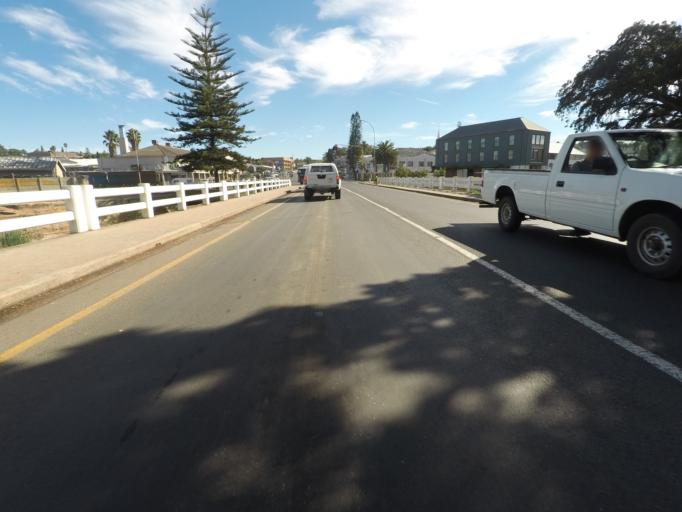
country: ZA
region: Western Cape
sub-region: West Coast District Municipality
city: Malmesbury
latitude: -33.4665
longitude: 18.7289
